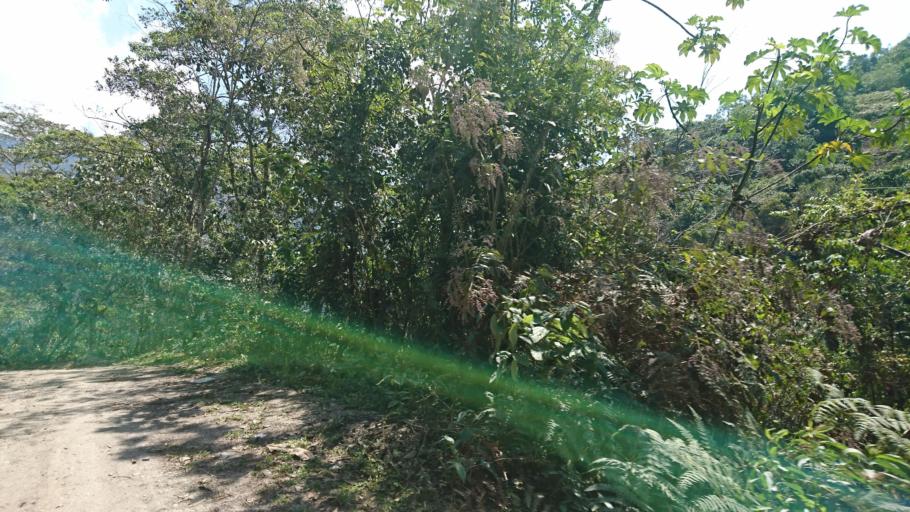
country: BO
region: La Paz
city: Coroico
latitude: -16.0396
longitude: -67.8136
